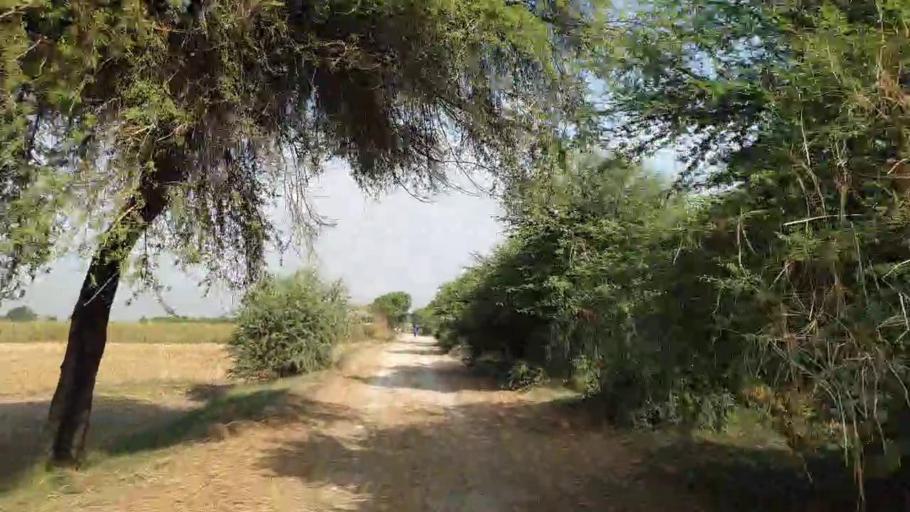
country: PK
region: Sindh
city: Tando Muhammad Khan
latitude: 25.0479
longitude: 68.4360
